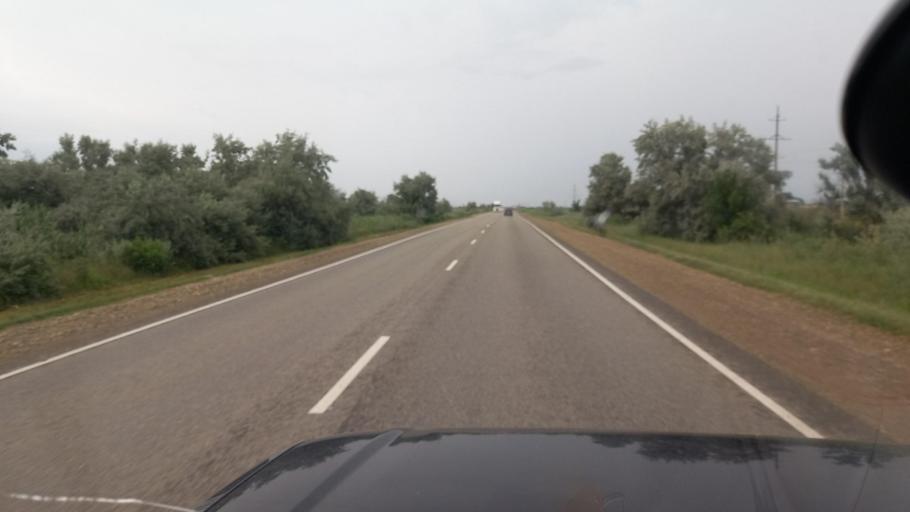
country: RU
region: Krasnodarskiy
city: Temryuk
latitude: 45.2748
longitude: 37.3422
